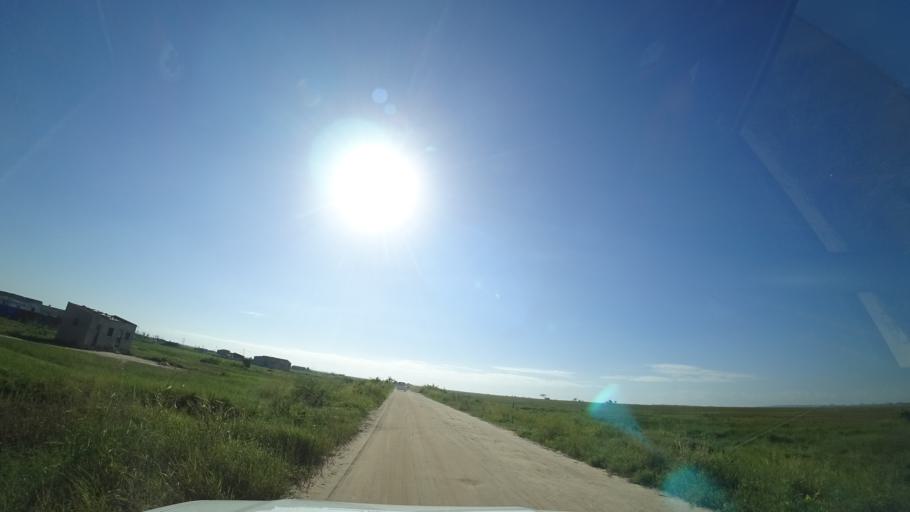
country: MZ
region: Sofala
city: Beira
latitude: -19.7613
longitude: 34.9105
